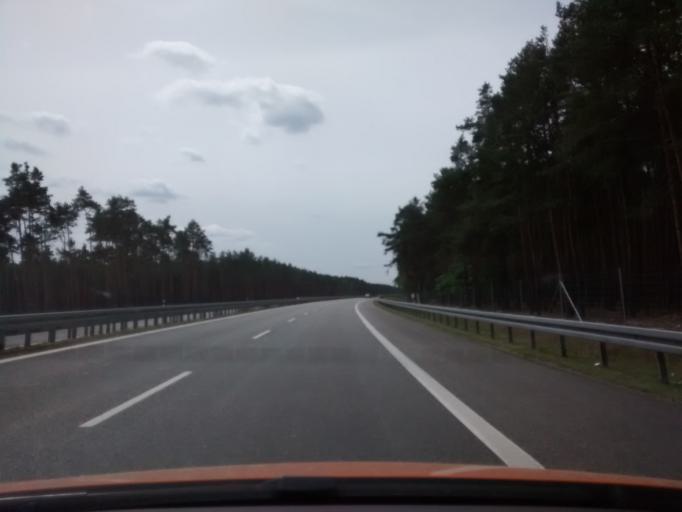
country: DE
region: Brandenburg
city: Trebbin
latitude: 52.1526
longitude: 13.2394
